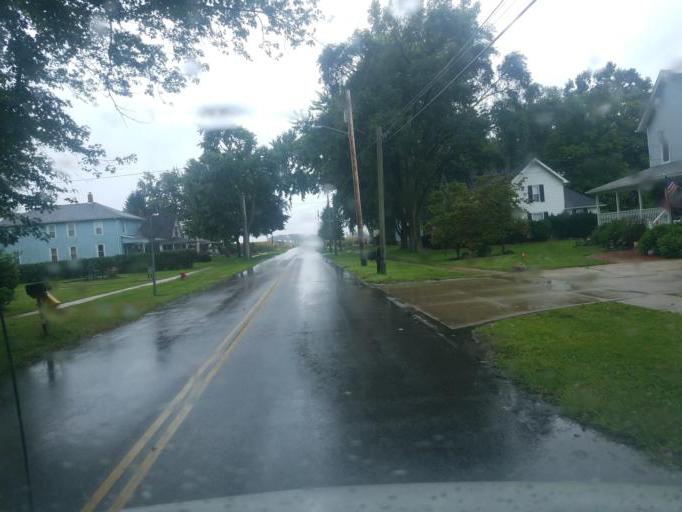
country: US
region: Ohio
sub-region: Medina County
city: Seville
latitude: 41.0082
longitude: -81.8615
